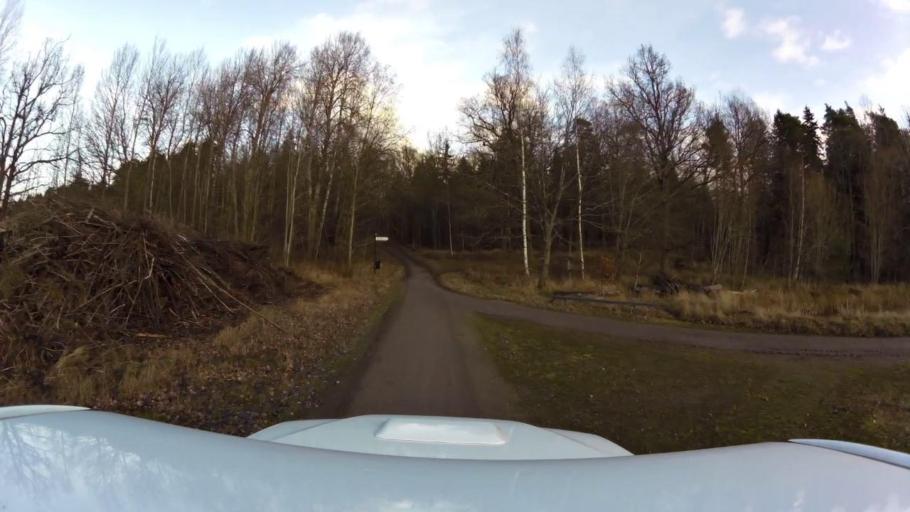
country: SE
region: OEstergoetland
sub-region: Linkopings Kommun
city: Linkoping
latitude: 58.3958
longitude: 15.5926
